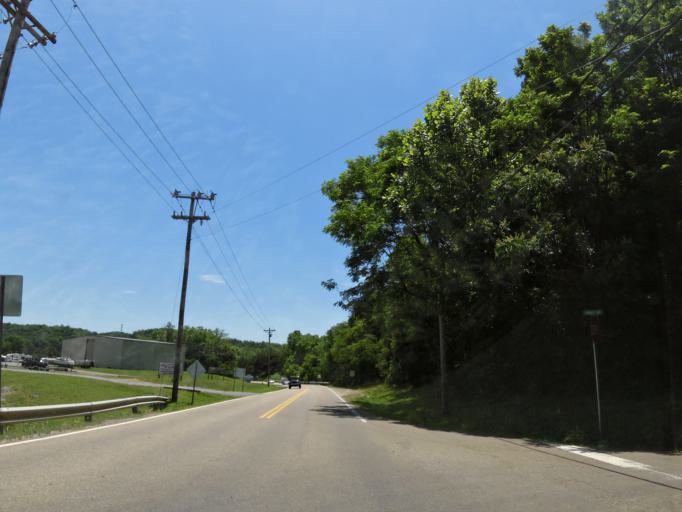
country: US
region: Tennessee
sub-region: Jefferson County
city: Dandridge
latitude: 36.0102
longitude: -83.4115
